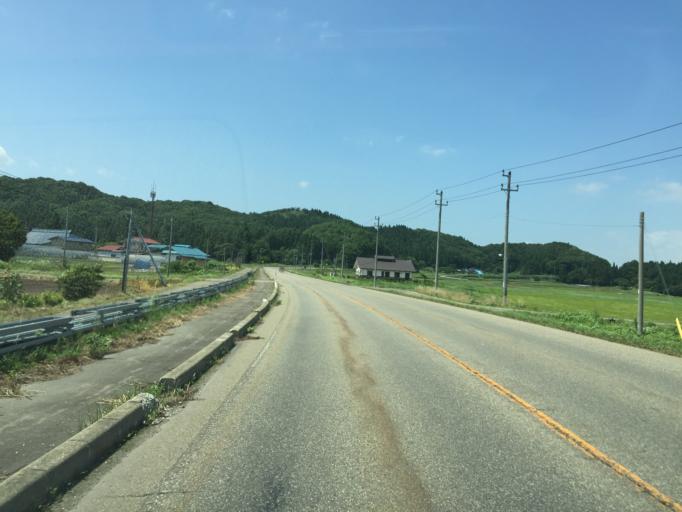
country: JP
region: Fukushima
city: Inawashiro
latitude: 37.4984
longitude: 140.0007
